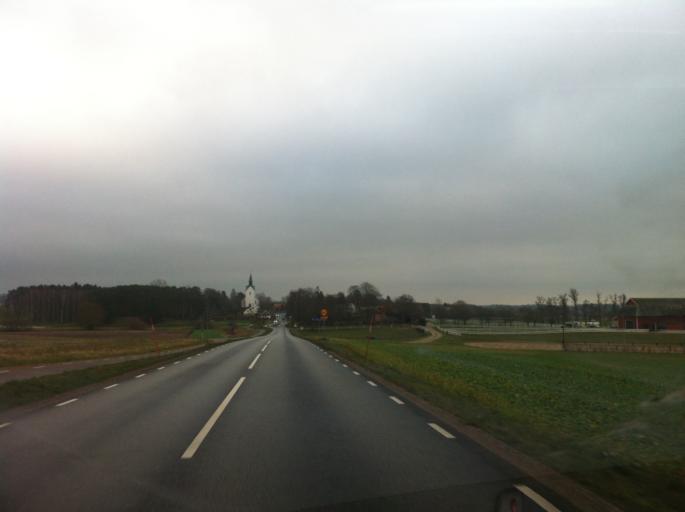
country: SE
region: Skane
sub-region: Hoors Kommun
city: Loberod
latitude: 55.7480
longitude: 13.3919
